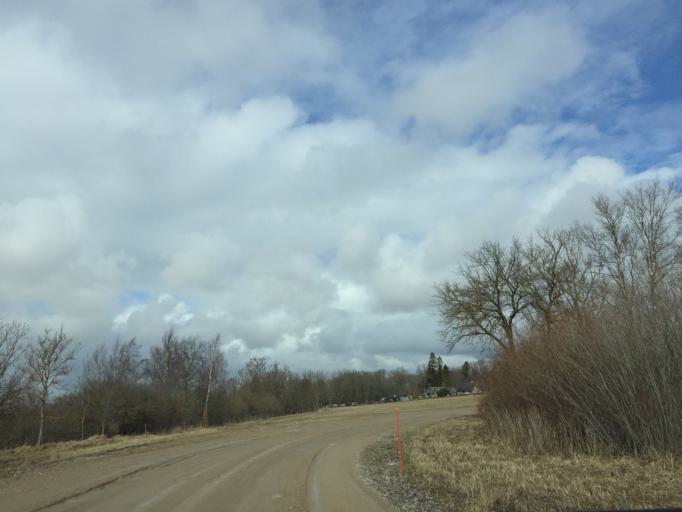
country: EE
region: Laeaene
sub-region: Lihula vald
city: Lihula
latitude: 58.7343
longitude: 23.8277
